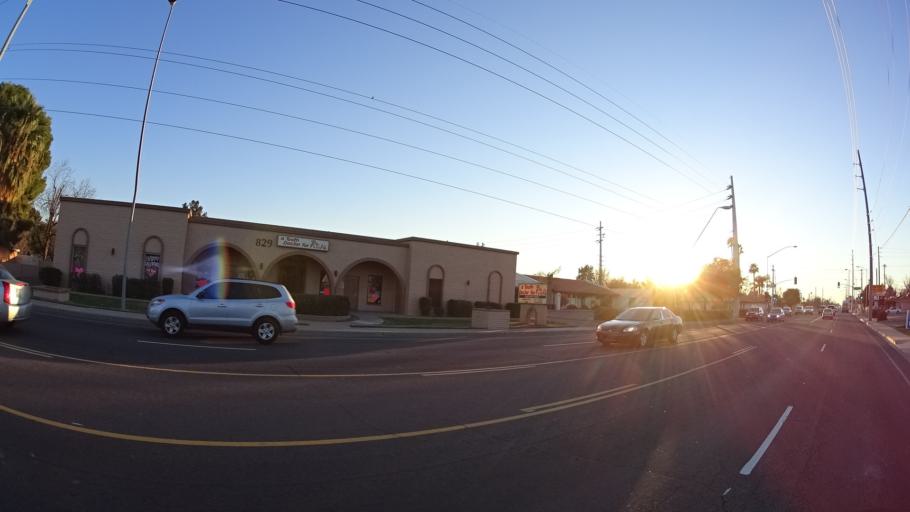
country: US
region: Arizona
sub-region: Maricopa County
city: Mesa
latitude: 33.4224
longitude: -111.8130
